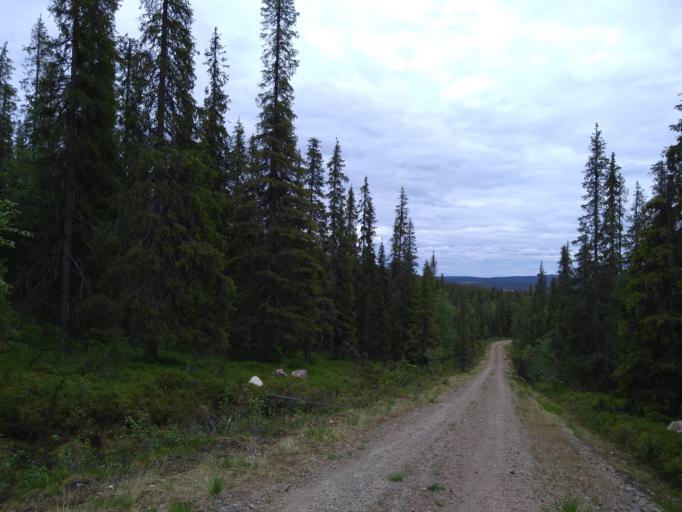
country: FI
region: Lapland
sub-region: Tunturi-Lappi
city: Muonio
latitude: 67.9654
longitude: 24.0789
